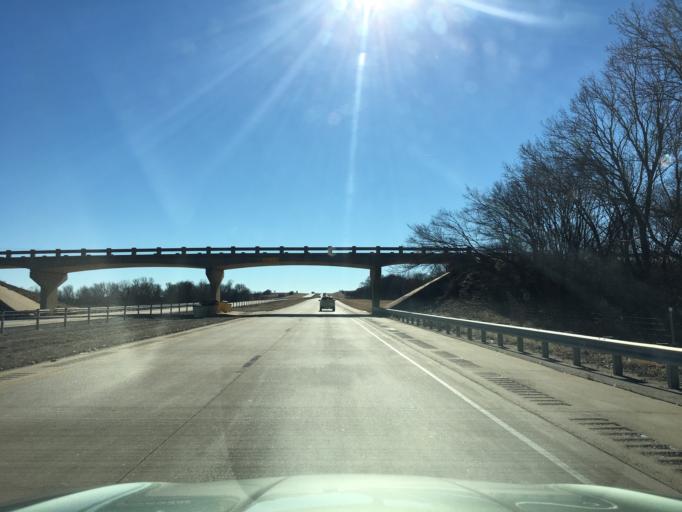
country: US
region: Oklahoma
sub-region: Noble County
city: Perry
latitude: 36.4644
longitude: -97.3271
